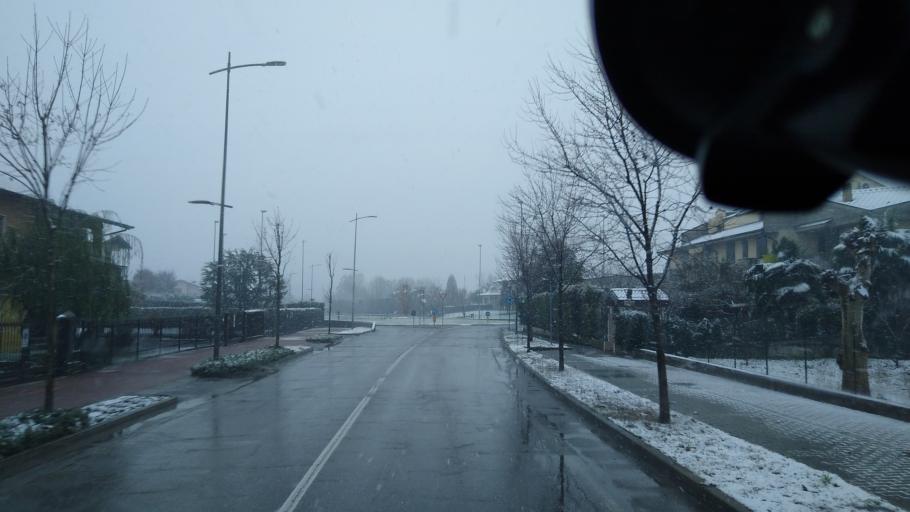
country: IT
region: Lombardy
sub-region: Provincia di Bergamo
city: Morengo
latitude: 45.5292
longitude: 9.7046
